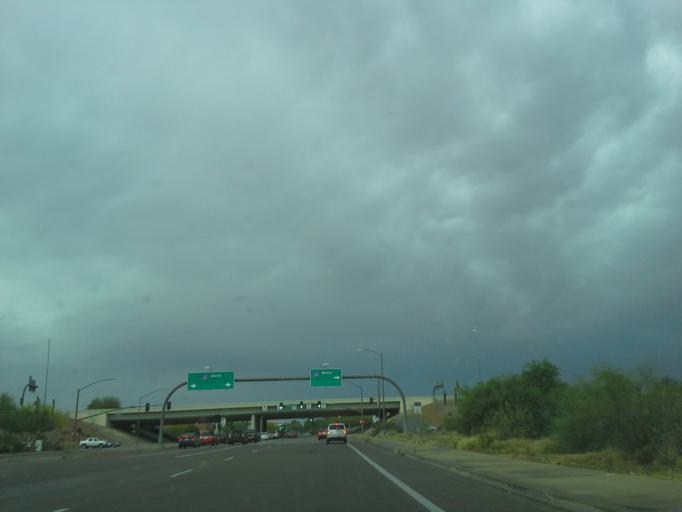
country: US
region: Arizona
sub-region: Maricopa County
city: Paradise Valley
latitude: 33.6402
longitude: -111.8882
